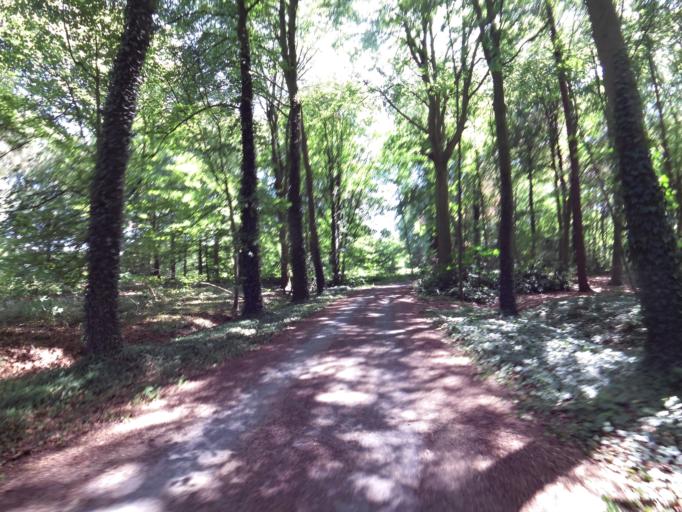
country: BE
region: Flanders
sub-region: Provincie West-Vlaanderen
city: Zedelgem
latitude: 51.1874
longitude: 3.1631
